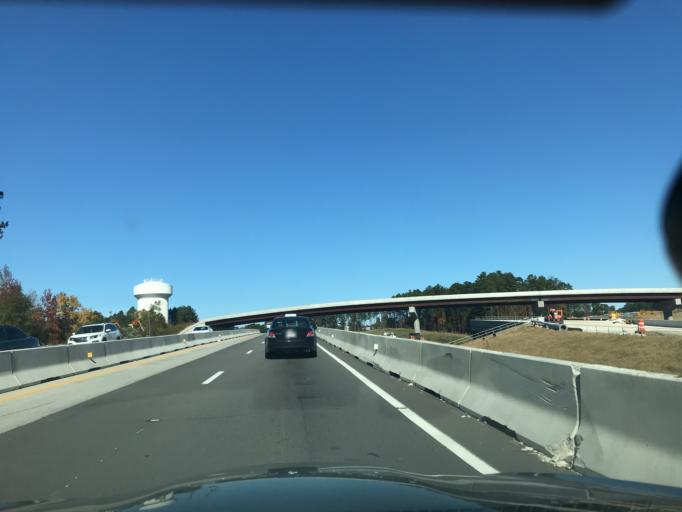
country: US
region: North Carolina
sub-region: Durham County
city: Durham
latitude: 35.9639
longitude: -78.8658
